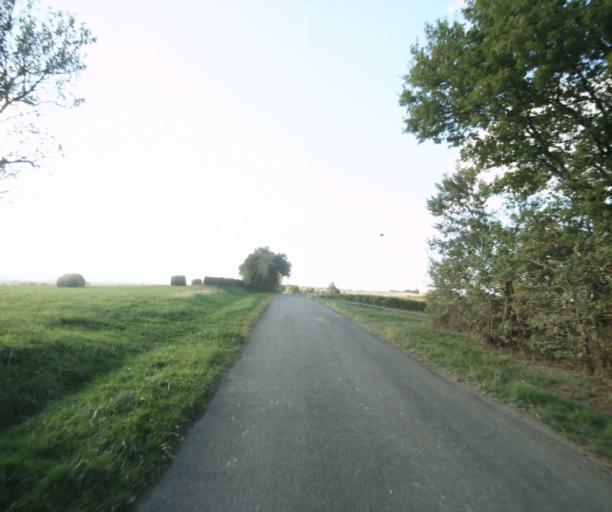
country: FR
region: Midi-Pyrenees
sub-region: Departement du Gers
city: Eauze
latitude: 43.7409
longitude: 0.1410
